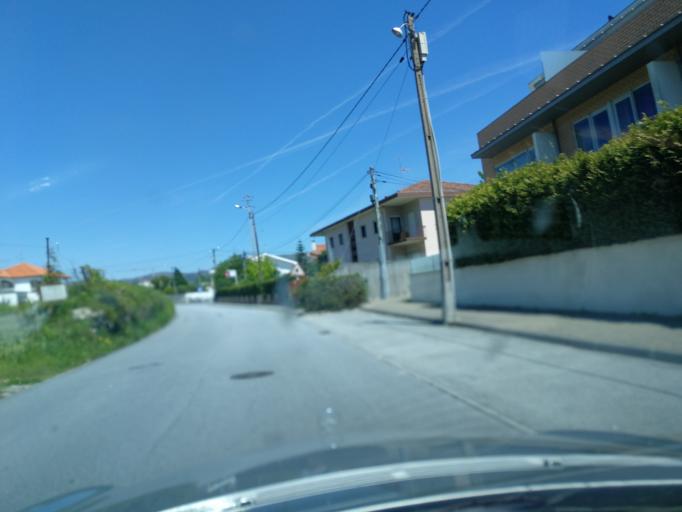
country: PT
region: Viana do Castelo
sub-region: Viana do Castelo
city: Meadela
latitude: 41.7145
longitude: -8.7998
